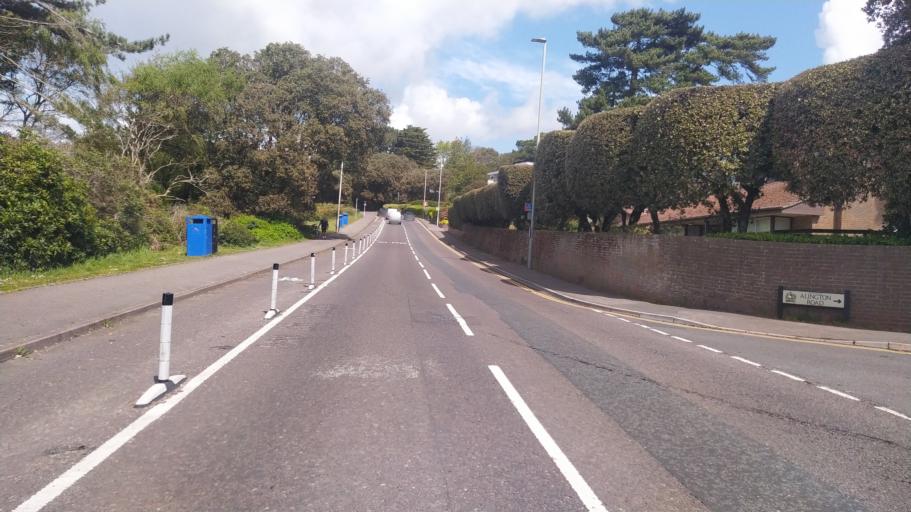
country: GB
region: England
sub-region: Dorset
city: Parkstone
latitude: 50.7022
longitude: -1.9414
